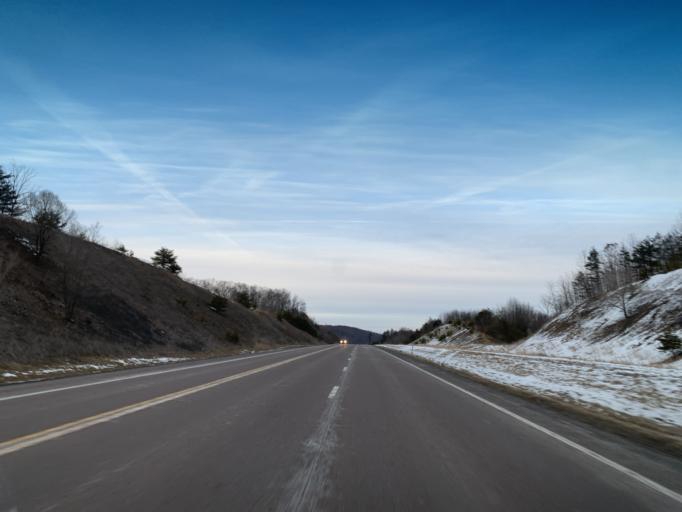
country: US
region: Maryland
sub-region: Allegany County
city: Cumberland
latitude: 39.7034
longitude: -78.7049
